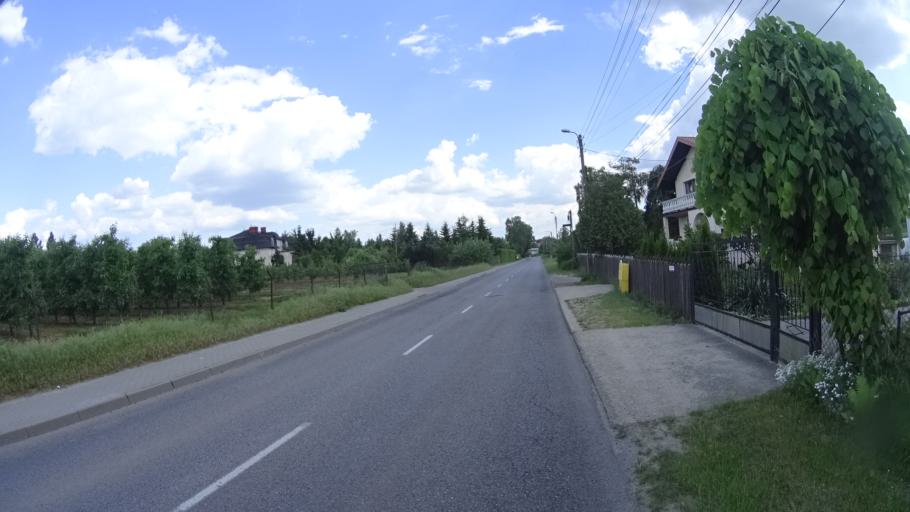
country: PL
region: Masovian Voivodeship
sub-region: Powiat piaseczynski
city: Tarczyn
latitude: 51.9858
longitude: 20.8281
